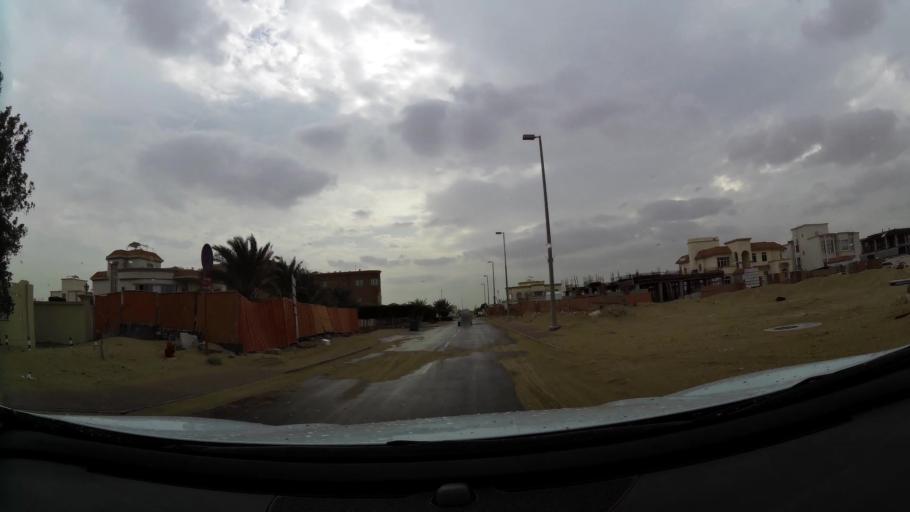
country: AE
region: Abu Dhabi
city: Abu Dhabi
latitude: 24.3637
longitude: 54.6243
